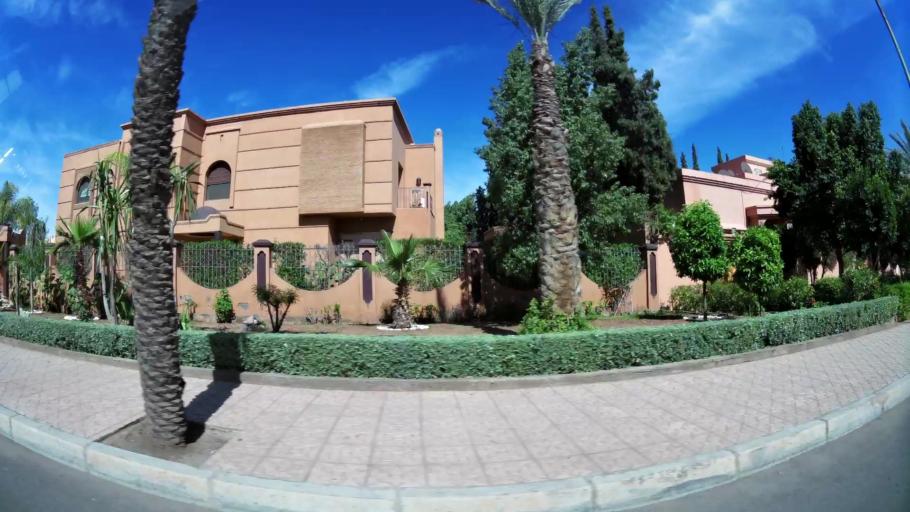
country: MA
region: Marrakech-Tensift-Al Haouz
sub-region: Marrakech
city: Marrakesh
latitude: 31.6430
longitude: -8.0469
